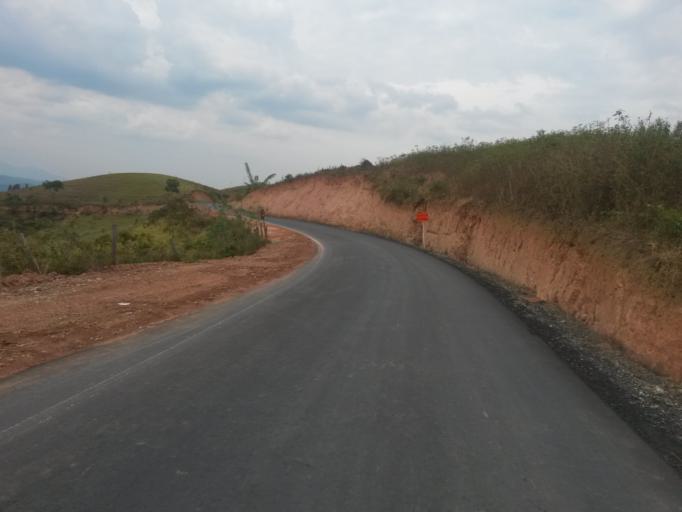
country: CO
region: Cauca
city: Buenos Aires
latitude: 3.0579
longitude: -76.6273
